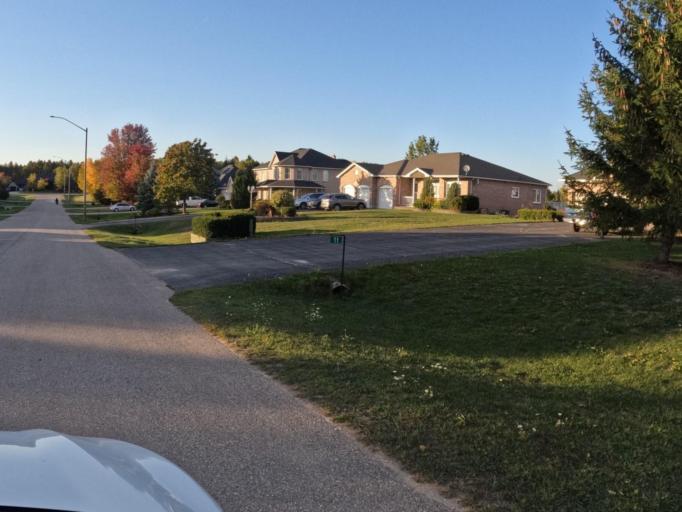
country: CA
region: Ontario
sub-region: Wellington County
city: Guelph
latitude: 43.4455
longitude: -80.1229
